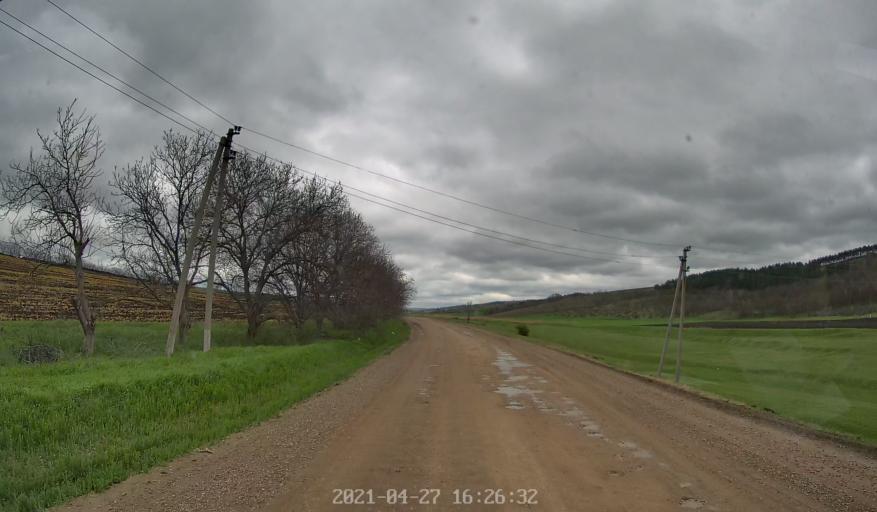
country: MD
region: Chisinau
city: Singera
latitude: 46.9793
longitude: 29.0268
